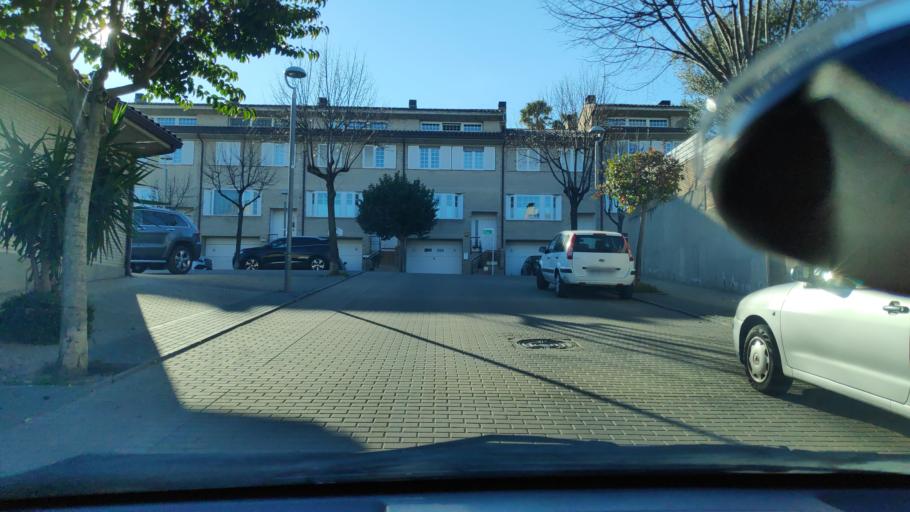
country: ES
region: Catalonia
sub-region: Provincia de Barcelona
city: Sant Quirze del Valles
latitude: 41.5298
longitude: 2.0691
